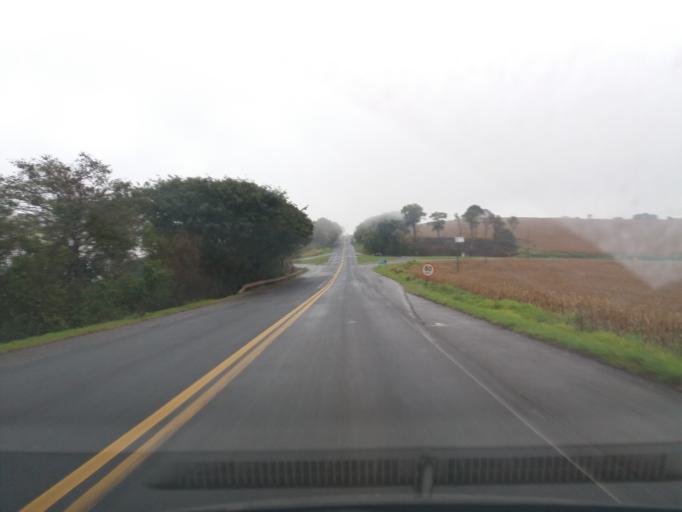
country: BR
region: Parana
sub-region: Ampere
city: Ampere
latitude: -25.8856
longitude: -53.4695
